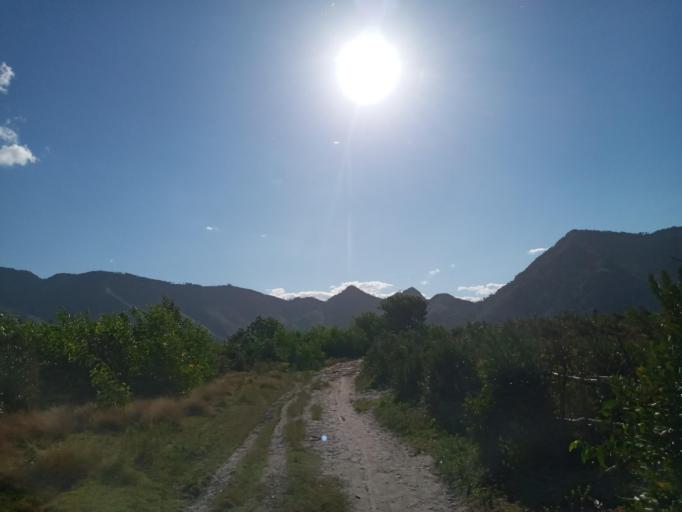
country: MG
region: Anosy
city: Fort Dauphin
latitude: -24.8294
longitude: 47.0492
